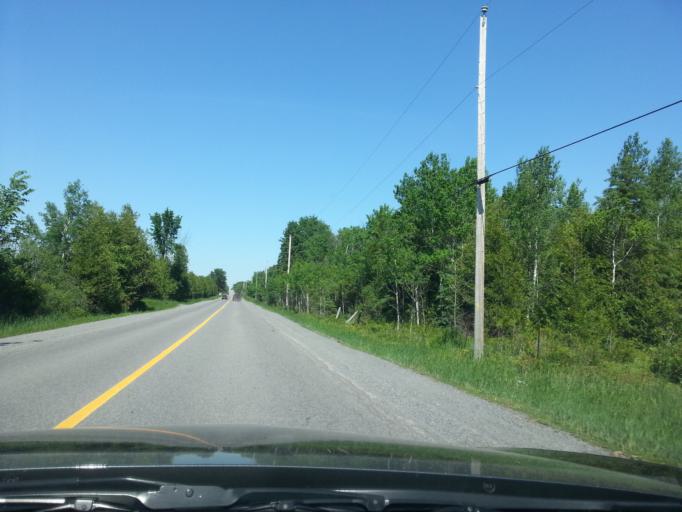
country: CA
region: Ontario
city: Carleton Place
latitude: 45.1937
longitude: -75.9999
